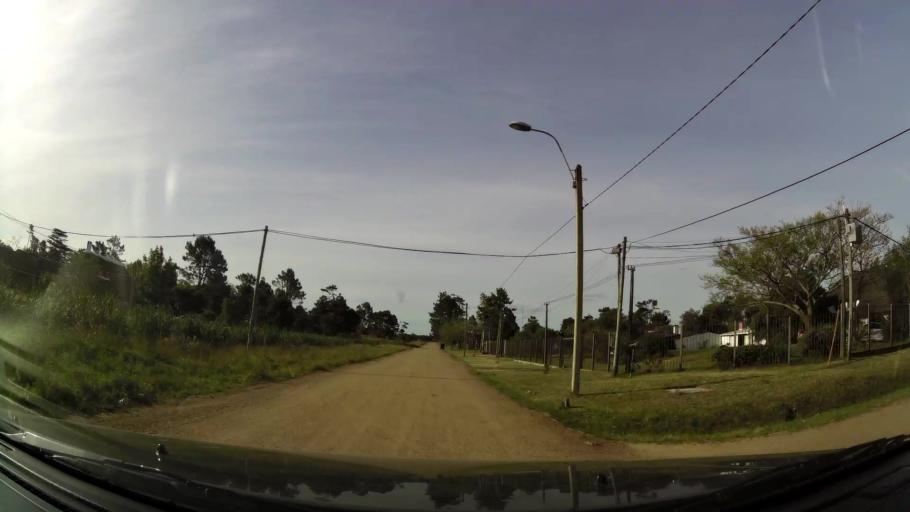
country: UY
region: Canelones
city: Atlantida
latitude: -34.7841
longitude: -55.8500
